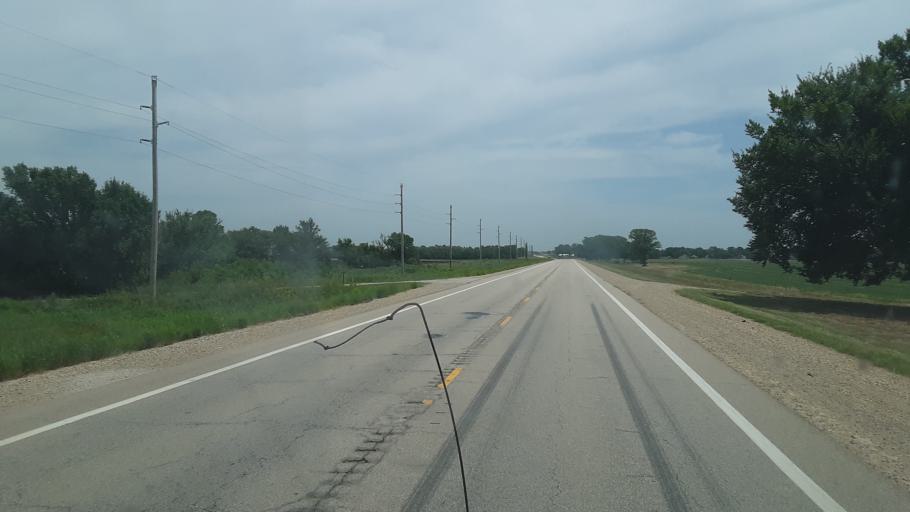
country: US
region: Kansas
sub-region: Greenwood County
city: Eureka
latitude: 37.8382
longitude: -96.0935
